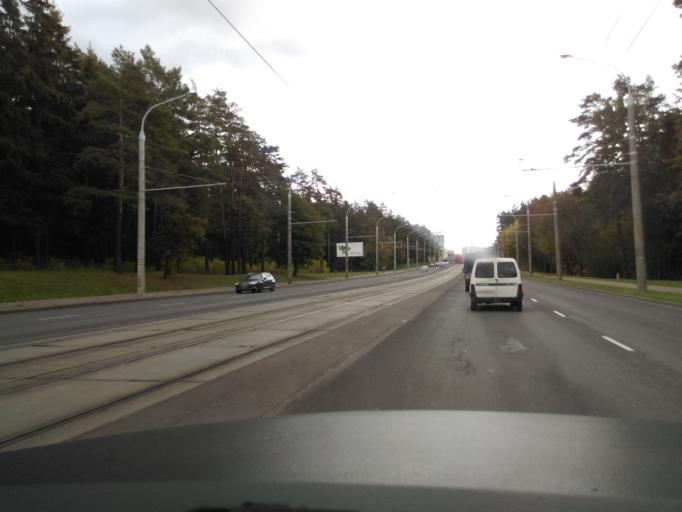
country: BY
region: Minsk
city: Minsk
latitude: 53.8810
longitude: 27.6240
